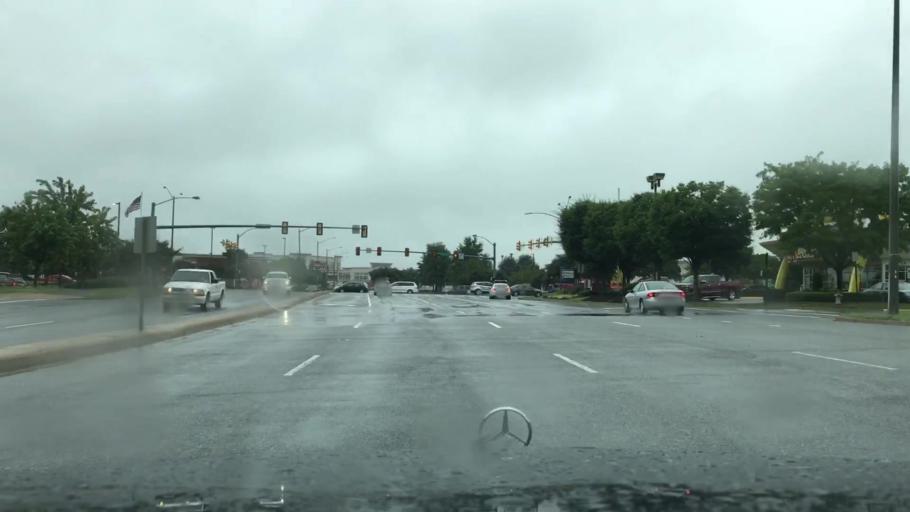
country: US
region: Virginia
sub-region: Stafford County
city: Falmouth
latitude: 38.3058
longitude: -77.5083
